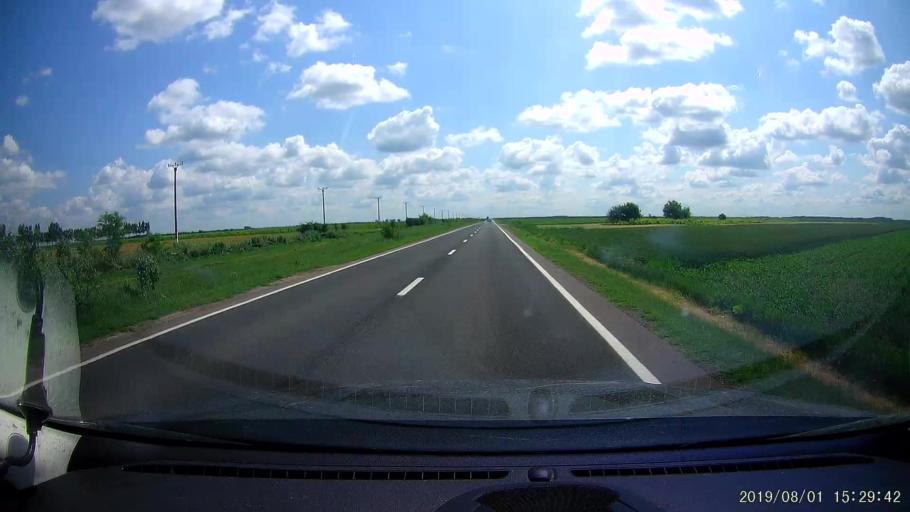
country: RO
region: Braila
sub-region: Comuna Viziru
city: Viziru
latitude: 44.9769
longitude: 27.6915
